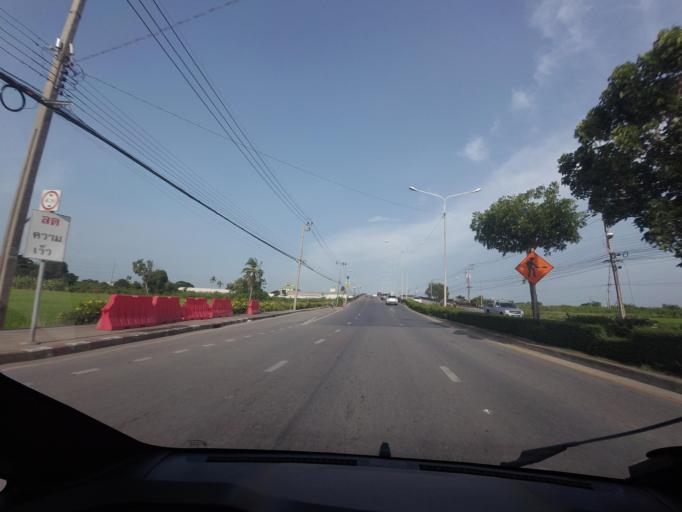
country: TH
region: Bangkok
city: Lat Krabang
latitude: 13.7030
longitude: 100.8413
